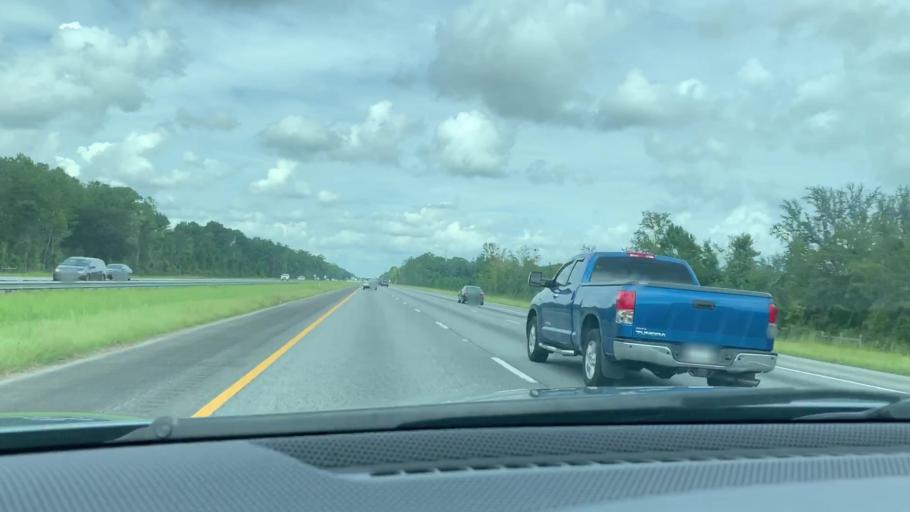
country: US
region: Georgia
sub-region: Liberty County
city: Midway
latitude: 31.6188
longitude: -81.4122
